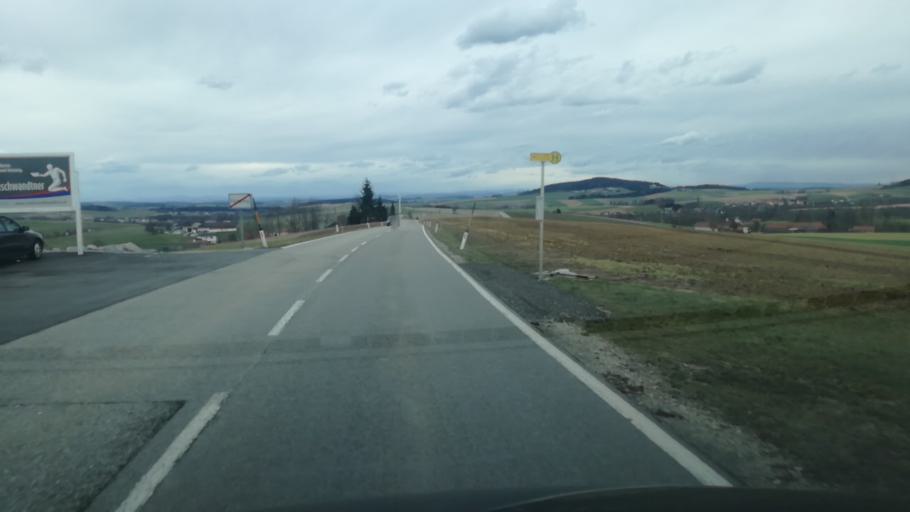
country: AT
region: Upper Austria
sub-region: Politischer Bezirk Vocklabruck
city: Frankenburg
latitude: 48.1169
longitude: 13.4876
